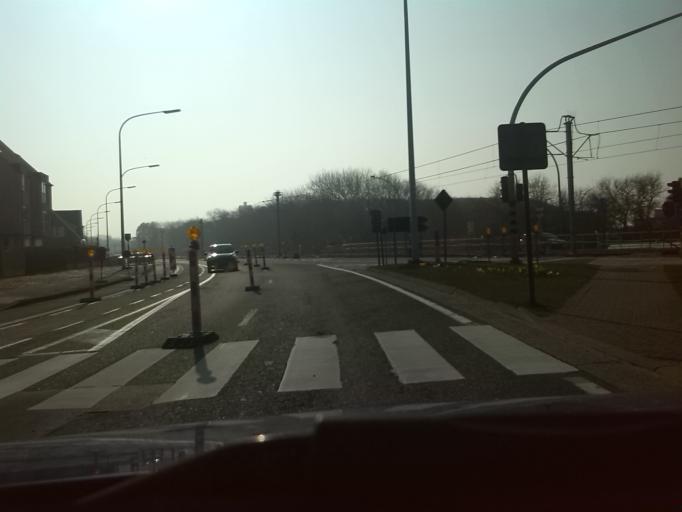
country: BE
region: Flanders
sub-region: Provincie West-Vlaanderen
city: Wenduine
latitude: 51.2964
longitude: 3.0765
